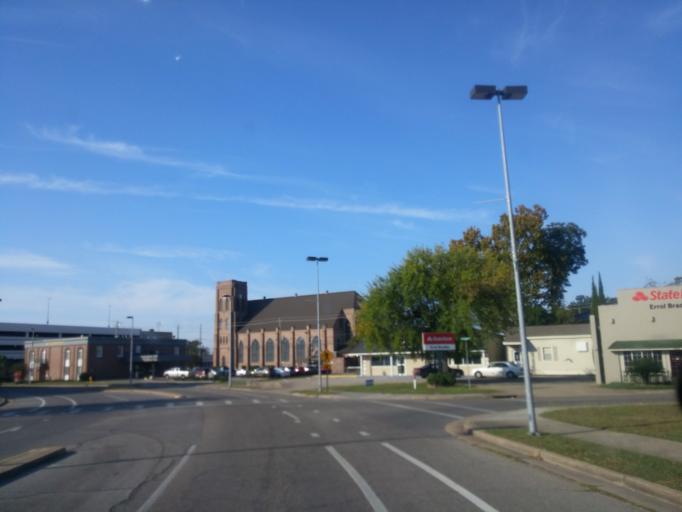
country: US
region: Mississippi
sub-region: Harrison County
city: Biloxi
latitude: 30.3979
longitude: -88.8899
